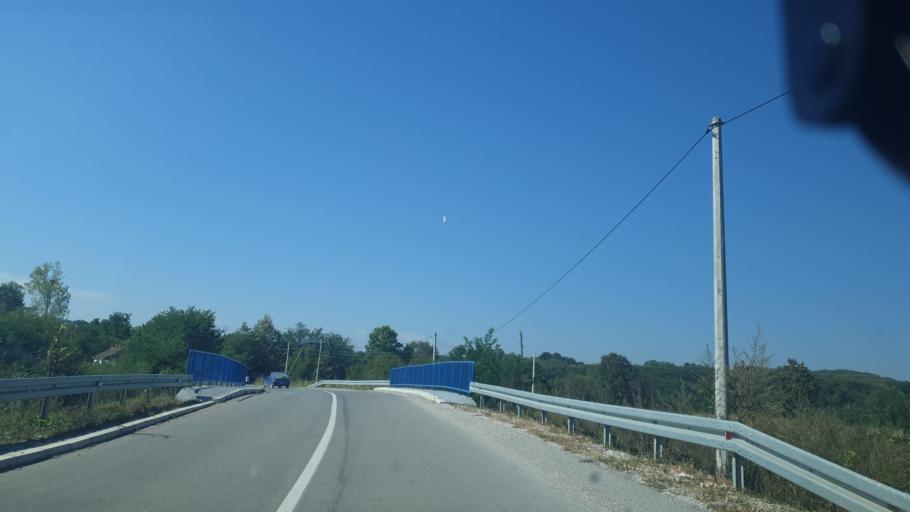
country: RS
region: Central Serbia
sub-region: Kolubarski Okrug
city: Mionica
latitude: 44.2856
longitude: 20.1120
